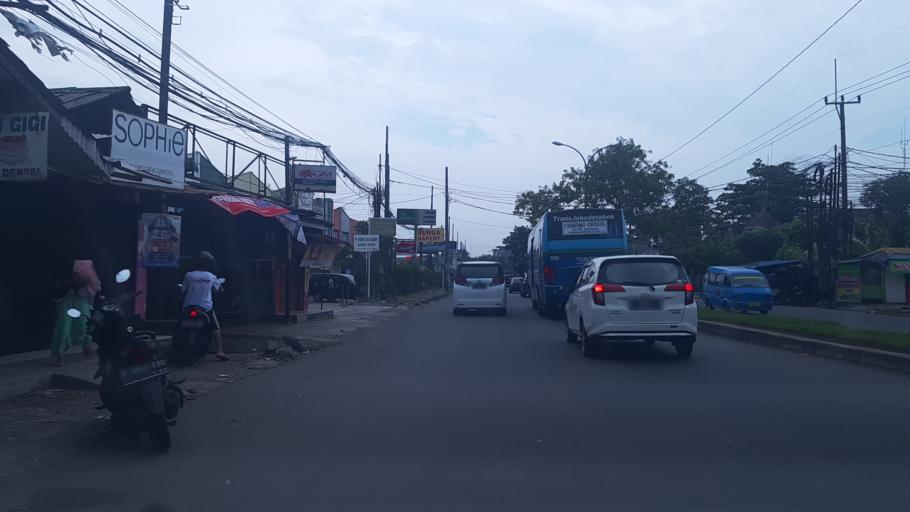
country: ID
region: West Java
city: Cibinong
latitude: -6.4770
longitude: 106.8634
